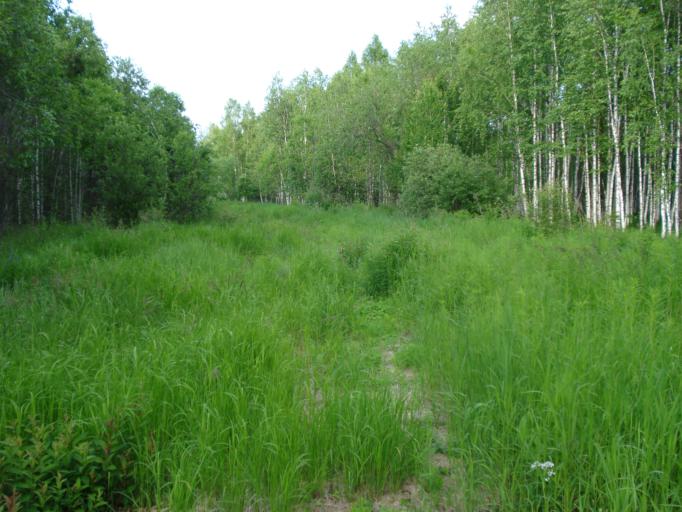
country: RU
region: Krasnoyarskiy
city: Predivinsk
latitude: 56.9760
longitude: 92.8903
